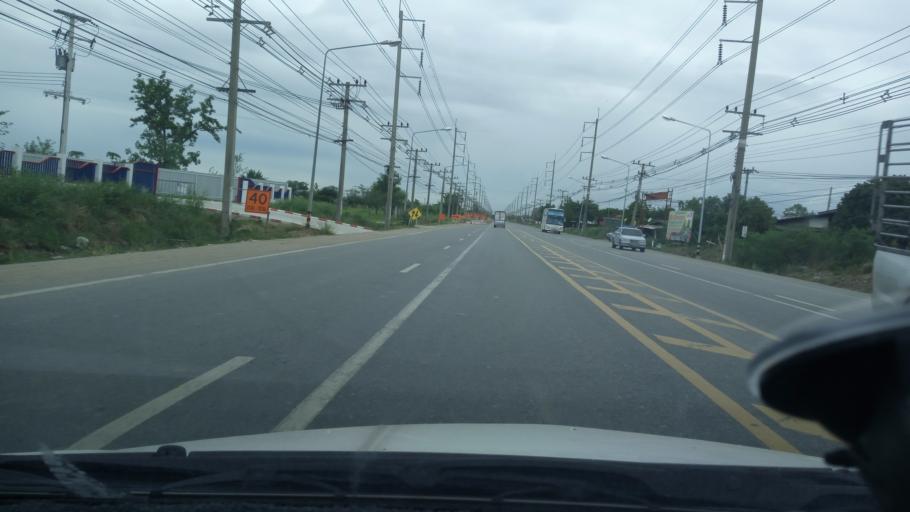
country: TH
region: Chon Buri
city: Phanat Nikhom
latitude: 13.4808
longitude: 101.1682
